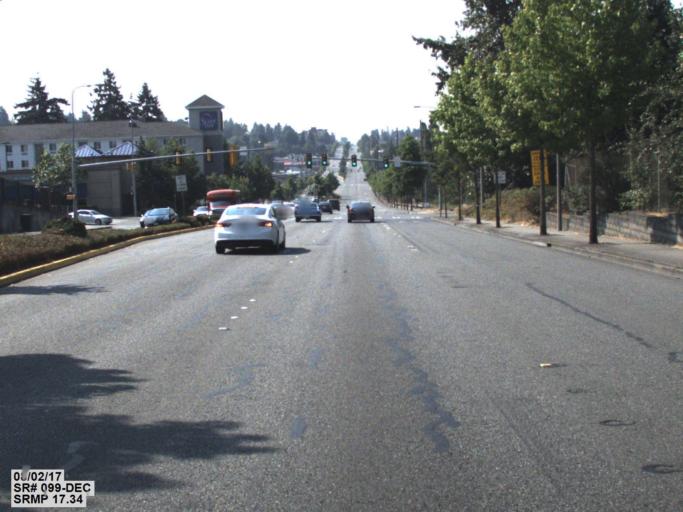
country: US
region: Washington
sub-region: King County
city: SeaTac
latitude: 47.4201
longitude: -122.2968
